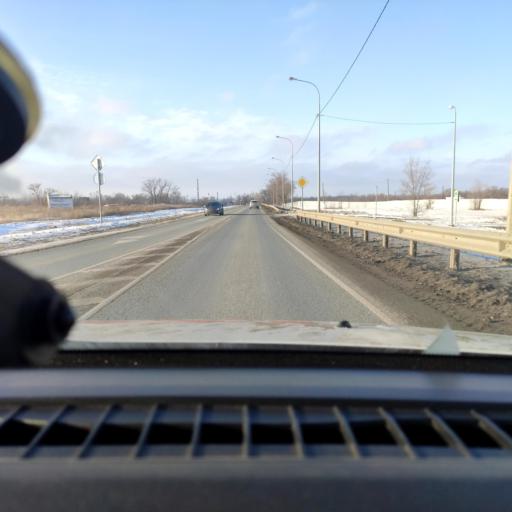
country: RU
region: Samara
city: Chapayevsk
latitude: 52.9971
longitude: 49.7337
